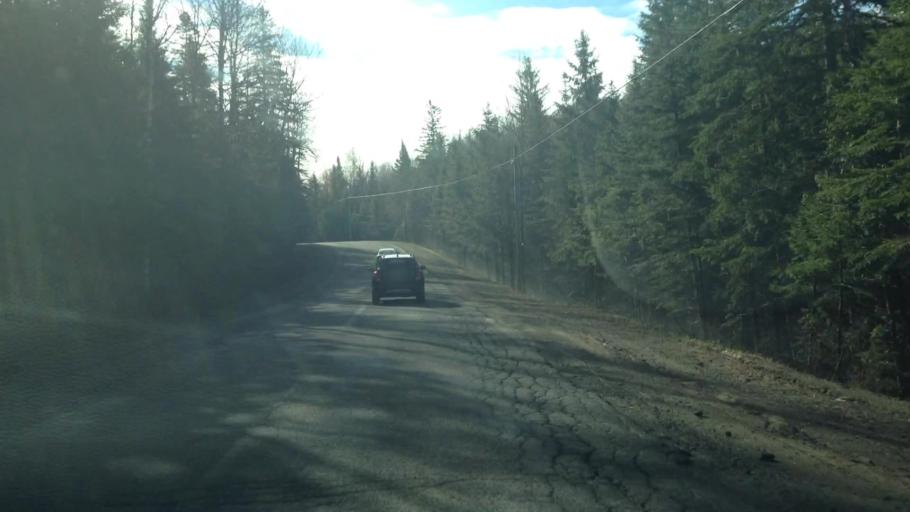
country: CA
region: Quebec
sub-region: Laurentides
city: Sainte-Adele
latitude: 46.0295
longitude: -74.0477
